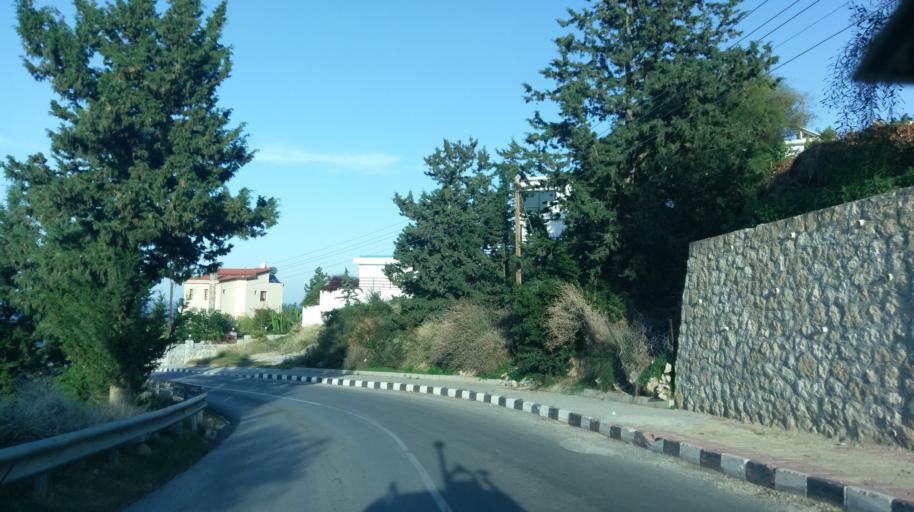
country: CY
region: Ammochostos
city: Lefkonoiko
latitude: 35.3430
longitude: 33.5786
